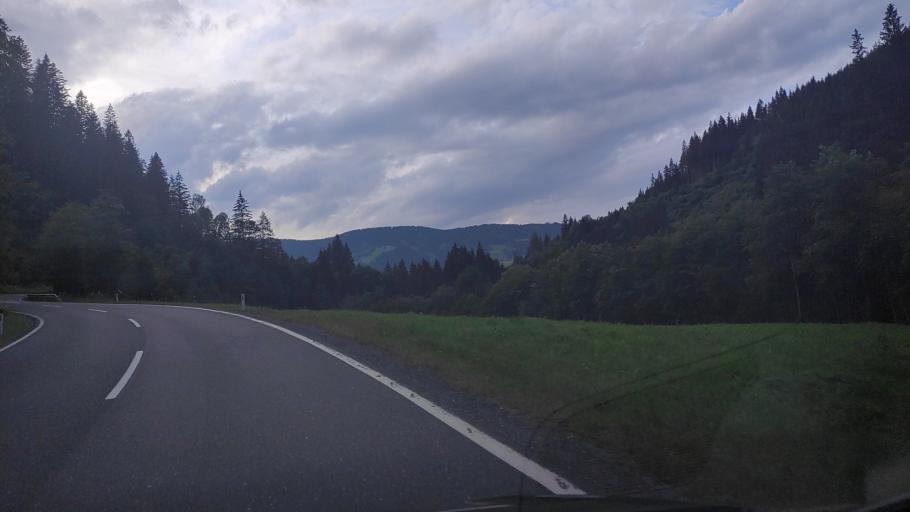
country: AT
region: Salzburg
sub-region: Politischer Bezirk Zell am See
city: Taxenbach
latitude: 47.2687
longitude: 12.9786
